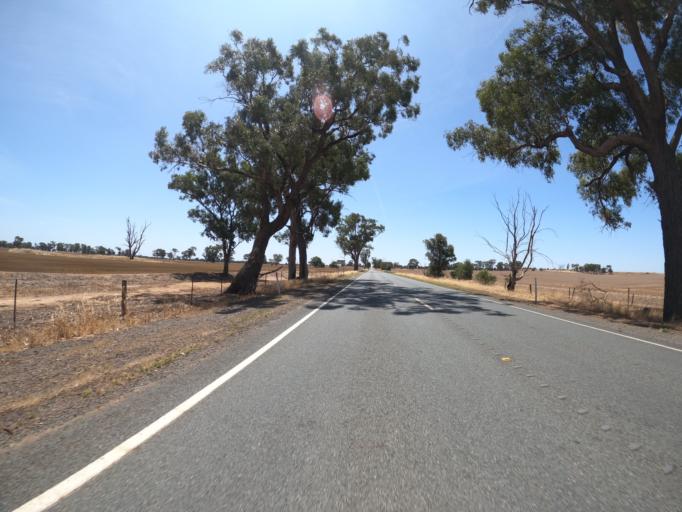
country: AU
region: Victoria
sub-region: Moira
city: Yarrawonga
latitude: -36.0594
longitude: 145.9954
